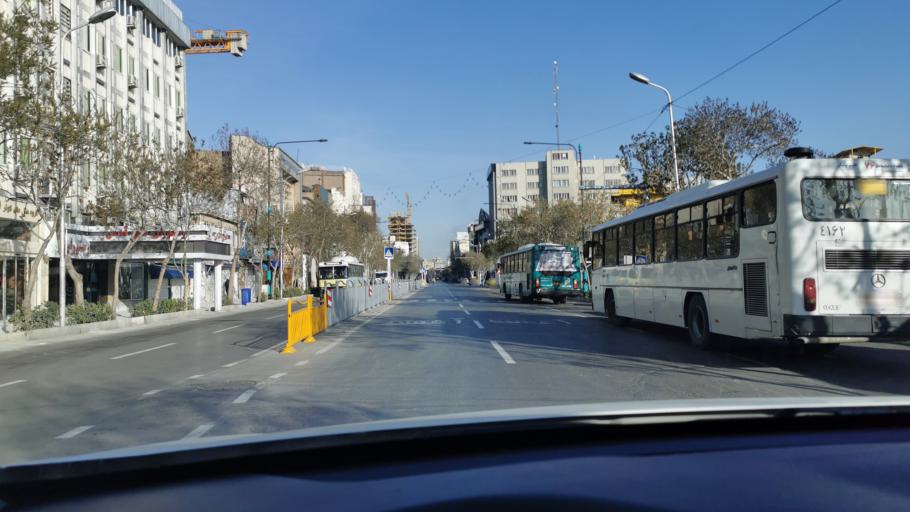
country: IR
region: Razavi Khorasan
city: Mashhad
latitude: 36.2851
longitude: 59.6112
